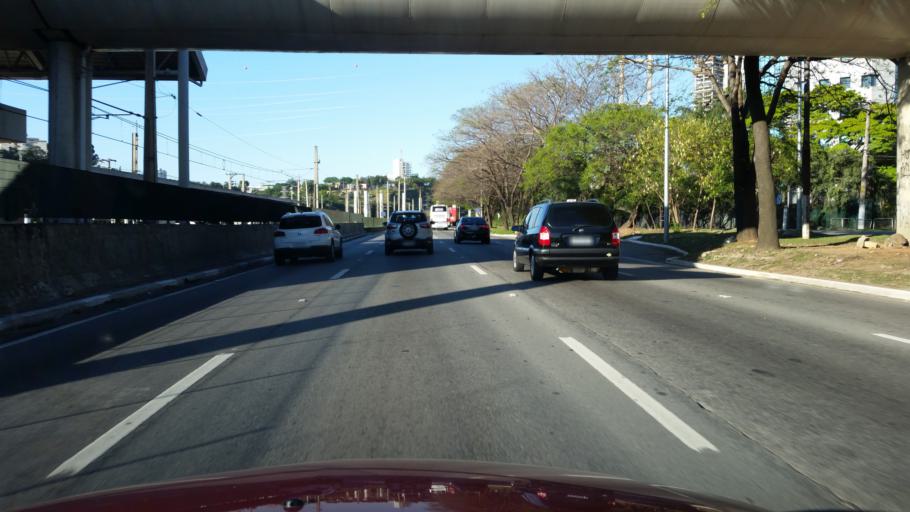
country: BR
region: Sao Paulo
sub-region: Taboao Da Serra
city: Taboao da Serra
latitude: -23.6283
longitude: -46.7123
